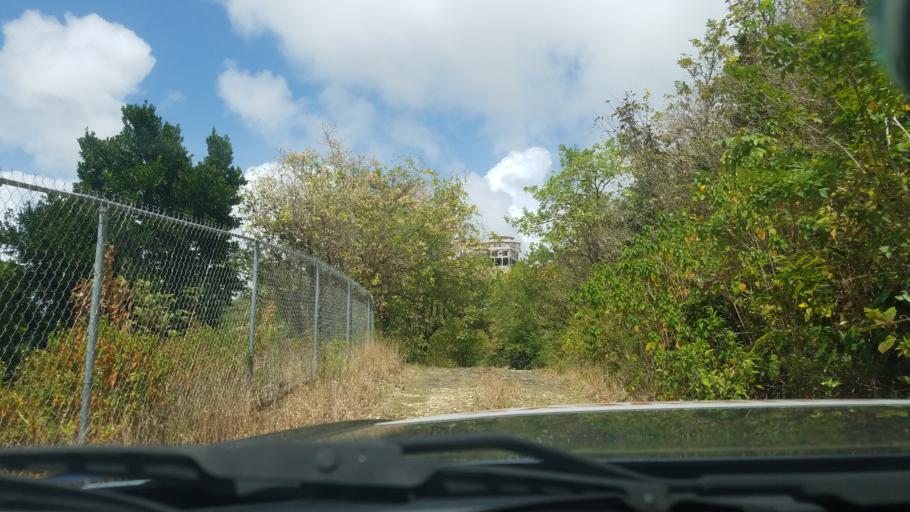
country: LC
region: Gros-Islet
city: Gros Islet
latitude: 14.0637
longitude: -60.9514
